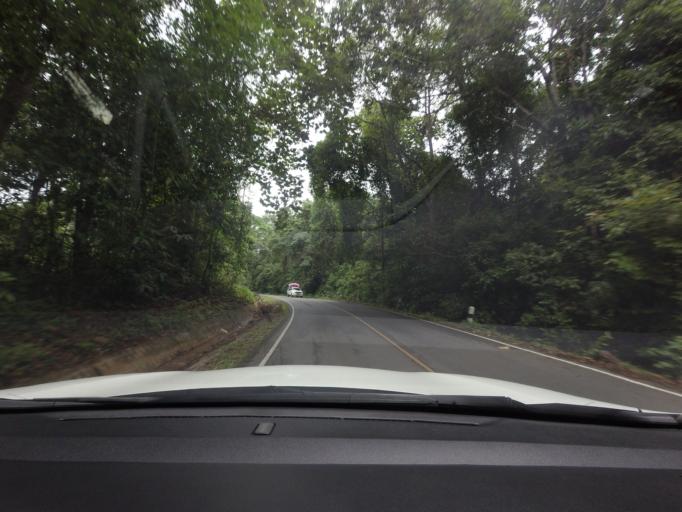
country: TH
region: Nakhon Ratchasima
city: Pak Chong
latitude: 14.4568
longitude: 101.3750
